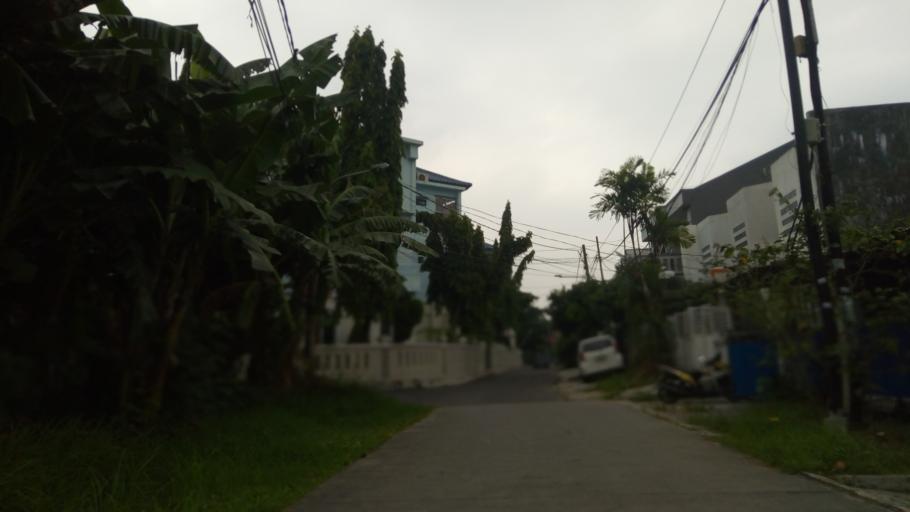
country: ID
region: Jakarta Raya
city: Jakarta
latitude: -6.1533
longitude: 106.8396
